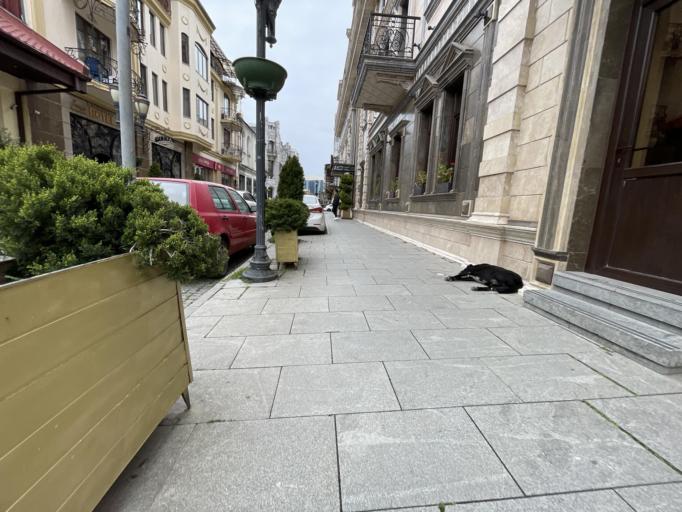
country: GE
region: Ajaria
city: Batumi
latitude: 41.6509
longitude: 41.6412
